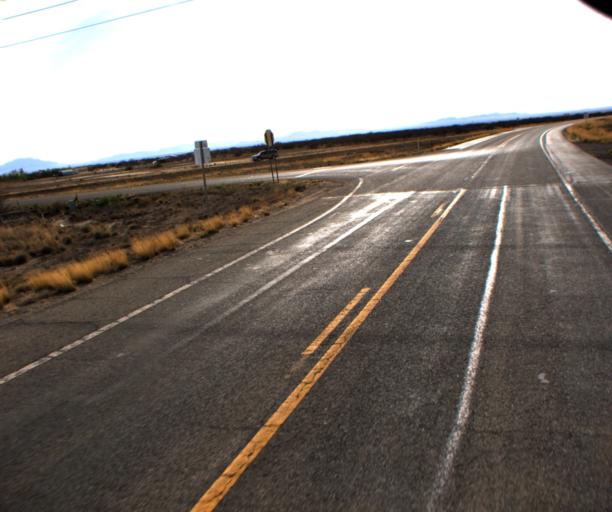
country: US
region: Arizona
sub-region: Cochise County
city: Willcox
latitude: 32.1953
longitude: -109.7557
